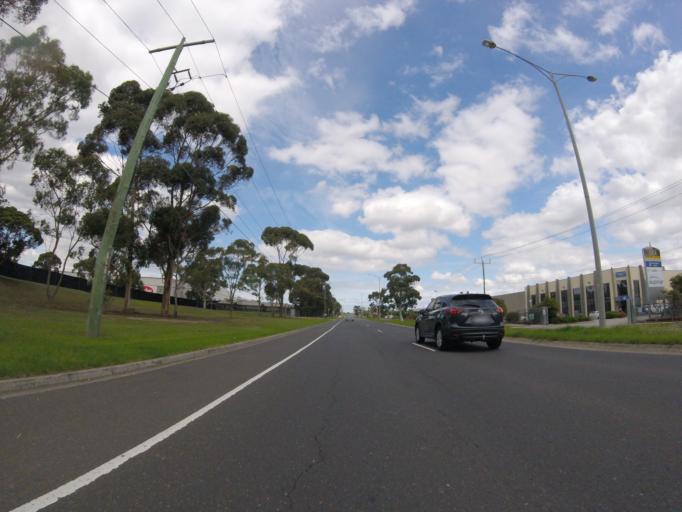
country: AU
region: Victoria
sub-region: Brimbank
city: Keilor Park
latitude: -37.7078
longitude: 144.8604
